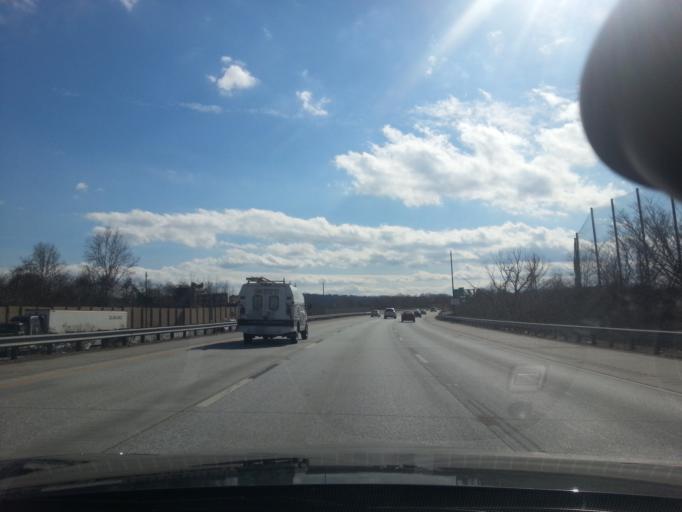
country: US
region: Pennsylvania
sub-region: Montgomery County
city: Conshohocken
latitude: 40.0850
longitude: -75.3104
